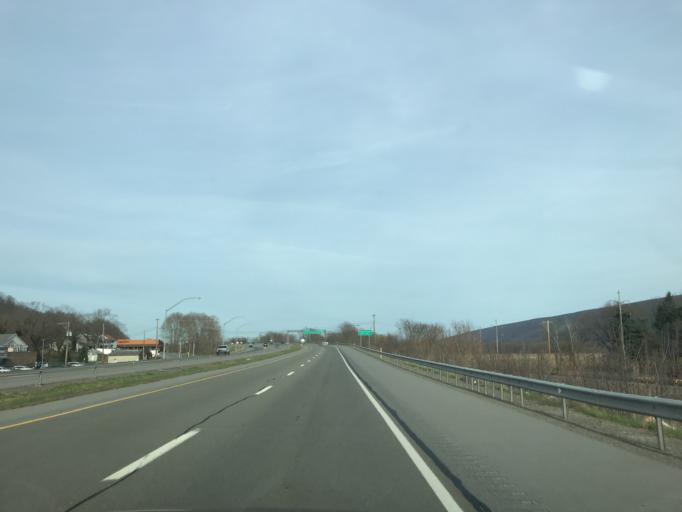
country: US
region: Pennsylvania
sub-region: Lycoming County
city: Kenmar
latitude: 41.2457
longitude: -76.9552
